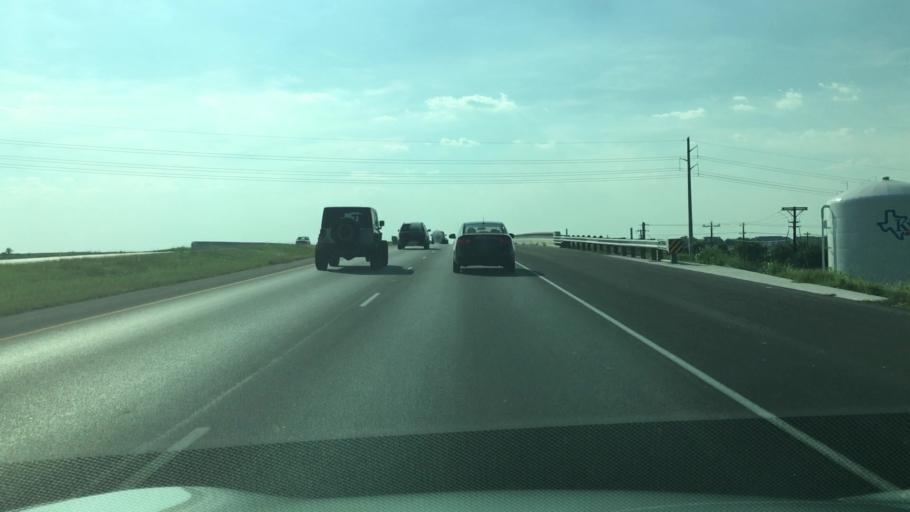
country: US
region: Texas
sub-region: Hays County
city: Kyle
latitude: 30.0165
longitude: -97.8675
